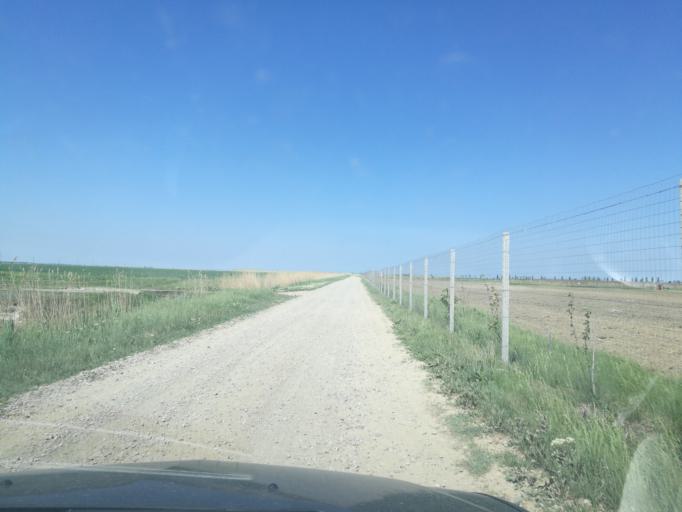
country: RO
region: Ialomita
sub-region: Comuna Adancata
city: Adancata
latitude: 44.7806
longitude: 26.4690
